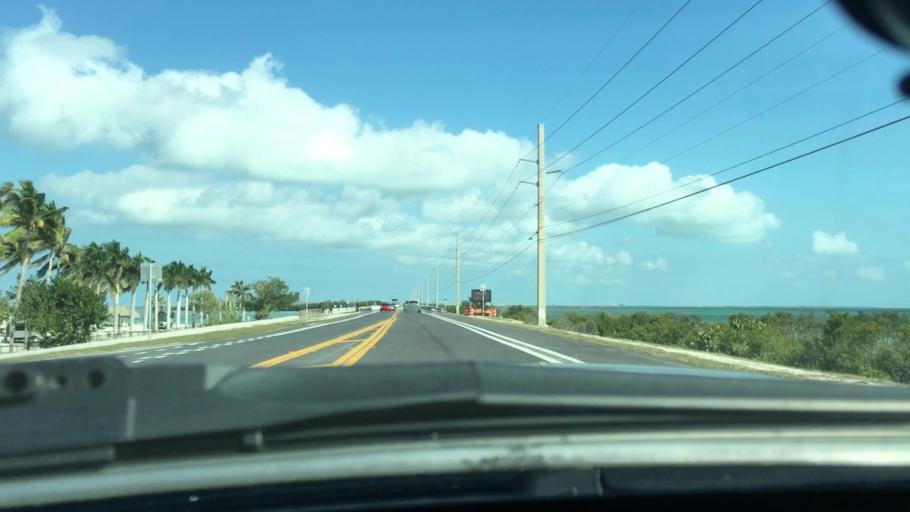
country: US
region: Florida
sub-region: Monroe County
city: Big Pine Key
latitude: 24.6725
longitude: -81.2453
